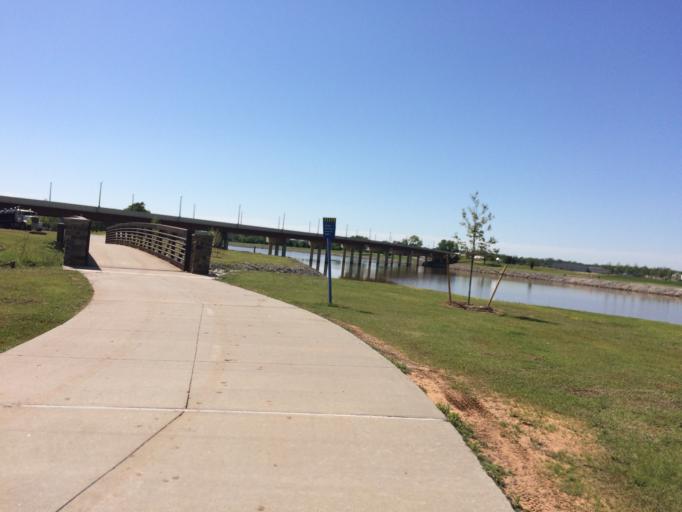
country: US
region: Oklahoma
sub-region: Oklahoma County
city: Oklahoma City
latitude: 35.4548
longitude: -97.5312
